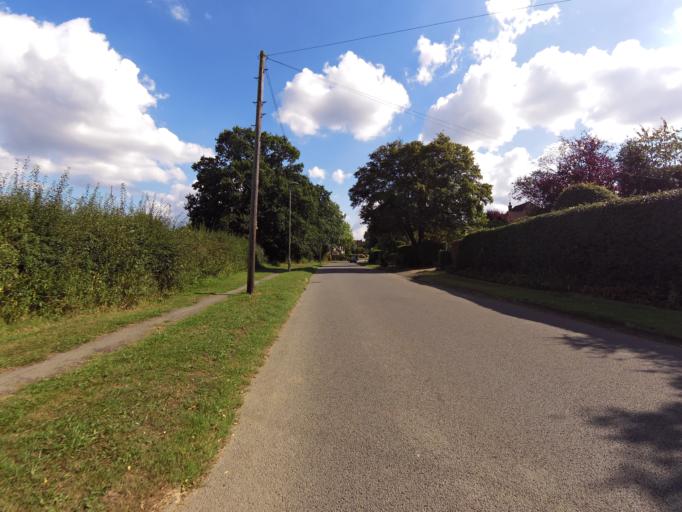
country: GB
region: England
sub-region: Greater London
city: High Barnet
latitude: 51.6558
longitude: -0.2246
